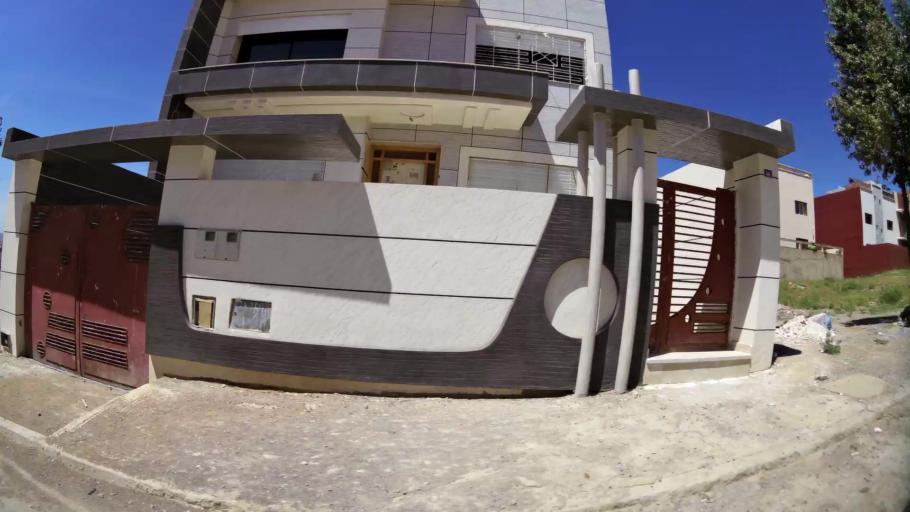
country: MA
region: Oriental
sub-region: Oujda-Angad
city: Oujda
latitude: 34.6549
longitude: -1.9186
